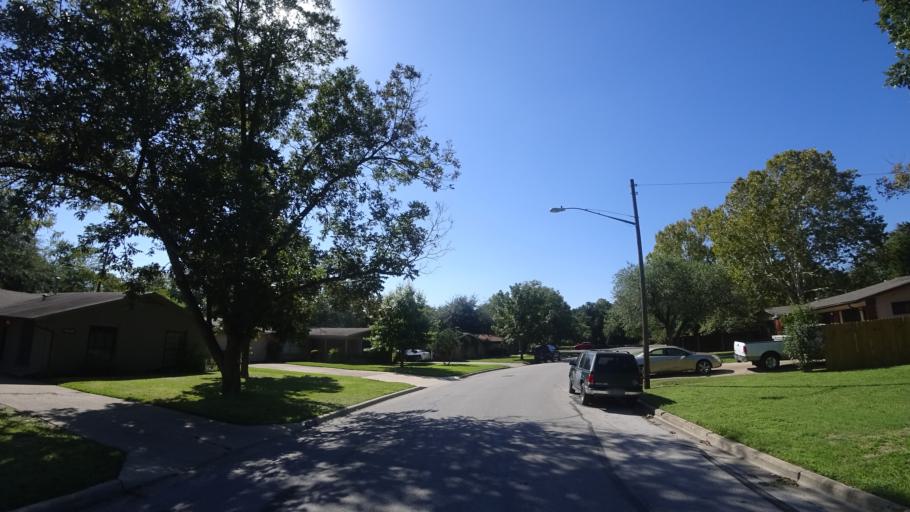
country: US
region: Texas
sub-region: Travis County
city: Austin
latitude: 30.3159
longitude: -97.6944
